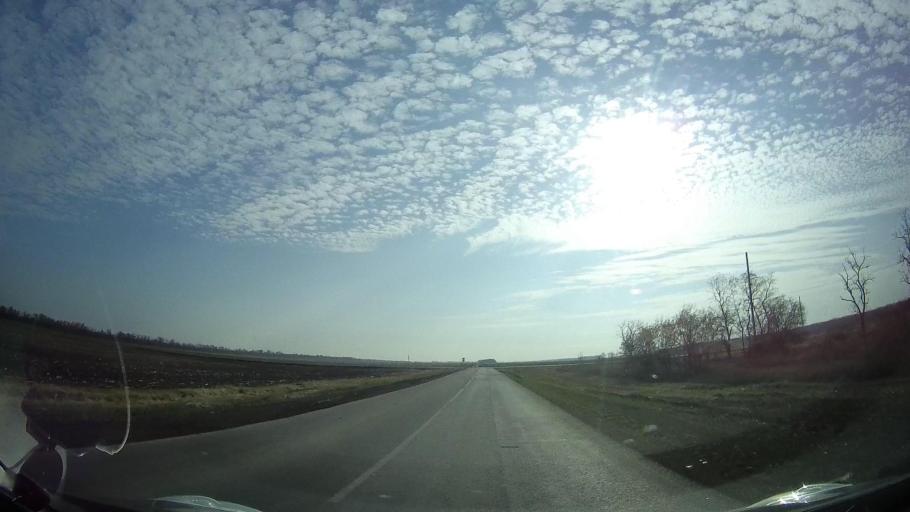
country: RU
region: Rostov
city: Veselyy
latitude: 46.9727
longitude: 40.7195
